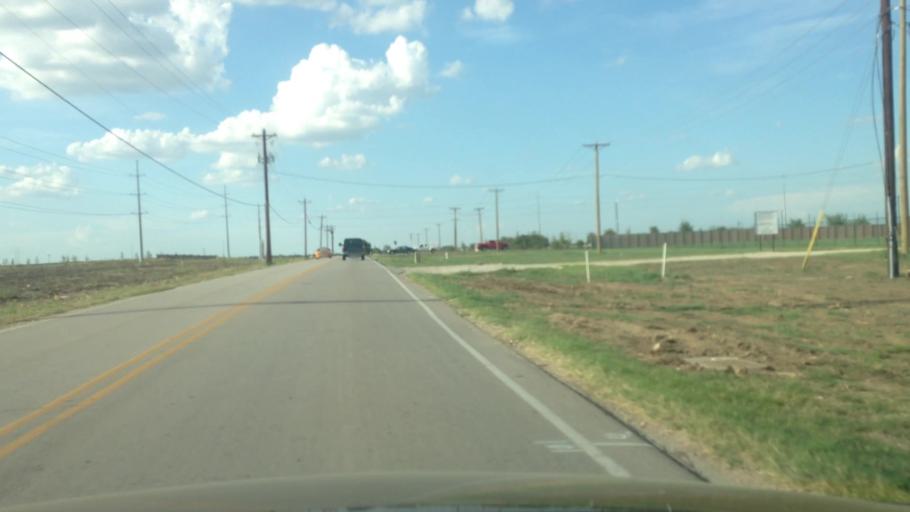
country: US
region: Texas
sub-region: Tarrant County
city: Haslet
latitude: 32.9414
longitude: -97.3920
